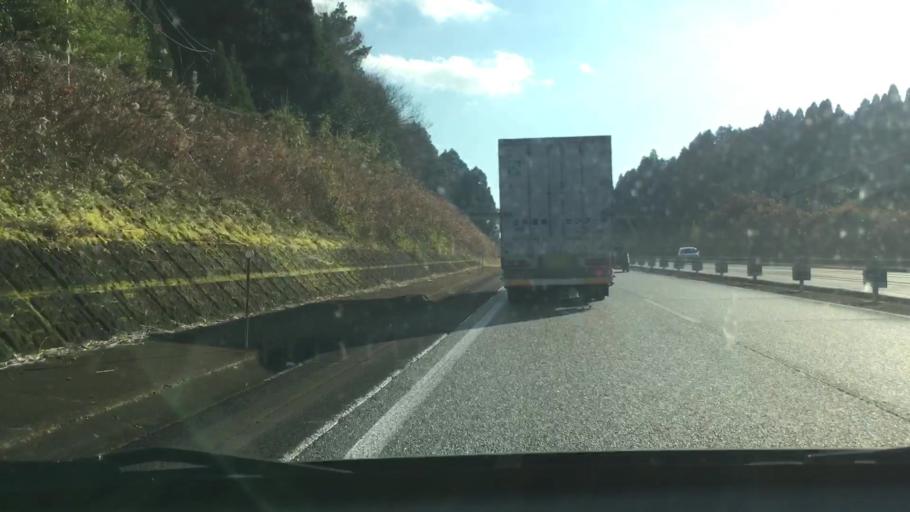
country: JP
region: Kagoshima
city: Okuchi-shinohara
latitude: 31.9299
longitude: 130.7051
